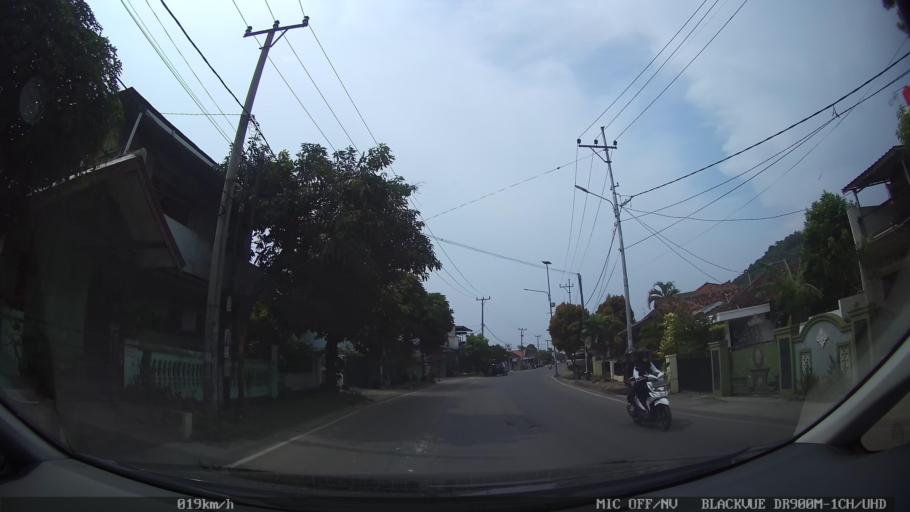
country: ID
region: Lampung
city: Bandarlampung
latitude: -5.4323
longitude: 105.2765
